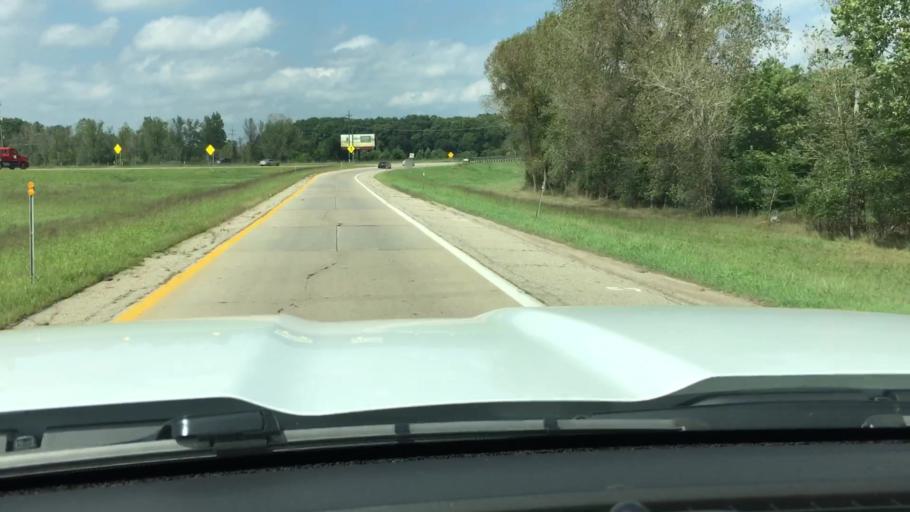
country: US
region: Michigan
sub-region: Allegan County
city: Plainwell
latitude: 42.4504
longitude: -85.6542
